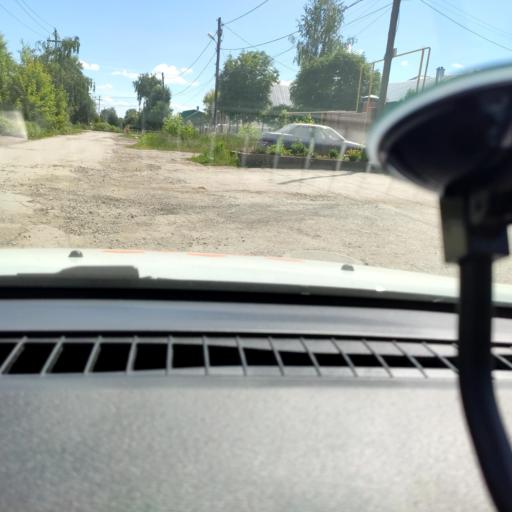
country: RU
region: Samara
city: Petra-Dubrava
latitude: 53.2496
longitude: 50.3316
